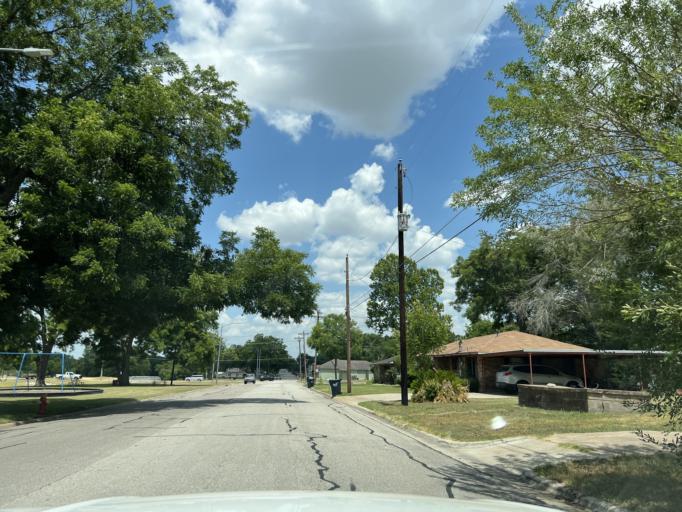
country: US
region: Texas
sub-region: Washington County
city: Brenham
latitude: 30.1686
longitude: -96.4075
